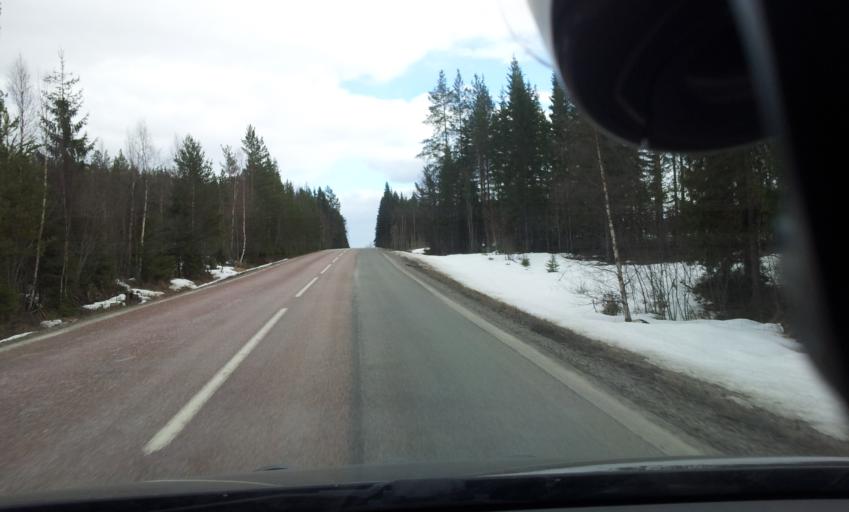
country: SE
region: Gaevleborg
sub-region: Ljusdals Kommun
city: Farila
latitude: 62.1234
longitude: 15.7202
